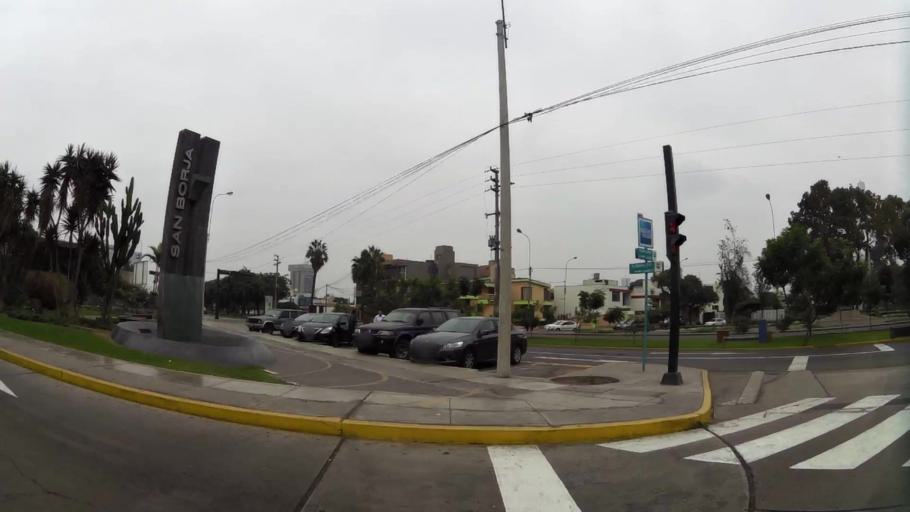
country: PE
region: Lima
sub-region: Lima
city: San Luis
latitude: -12.0938
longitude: -77.0097
